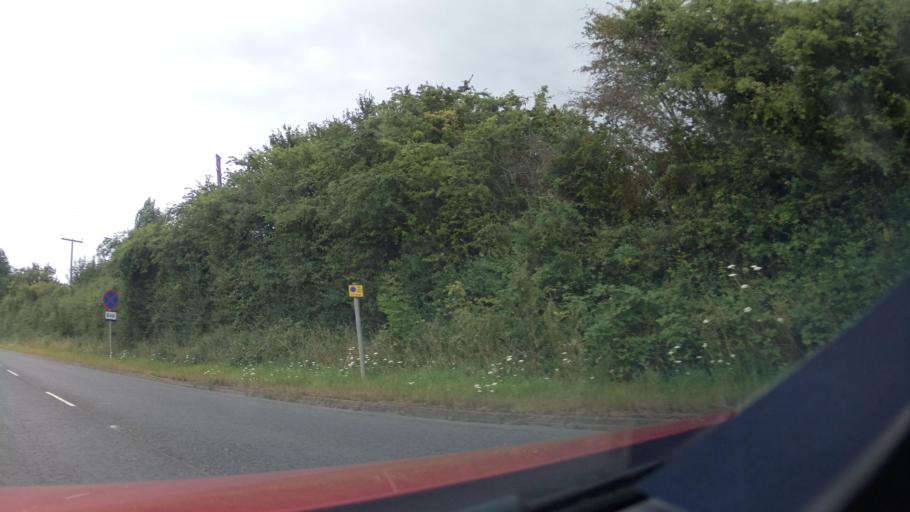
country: GB
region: England
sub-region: Worcestershire
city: Fernhill Heath
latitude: 52.2234
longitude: -2.1648
